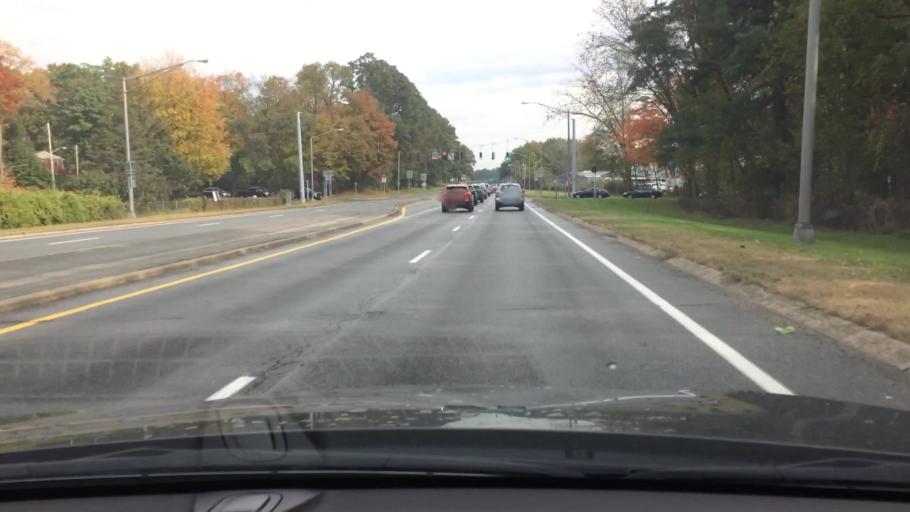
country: US
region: New York
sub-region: Saratoga County
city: Saratoga Springs
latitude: 43.0923
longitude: -73.7639
